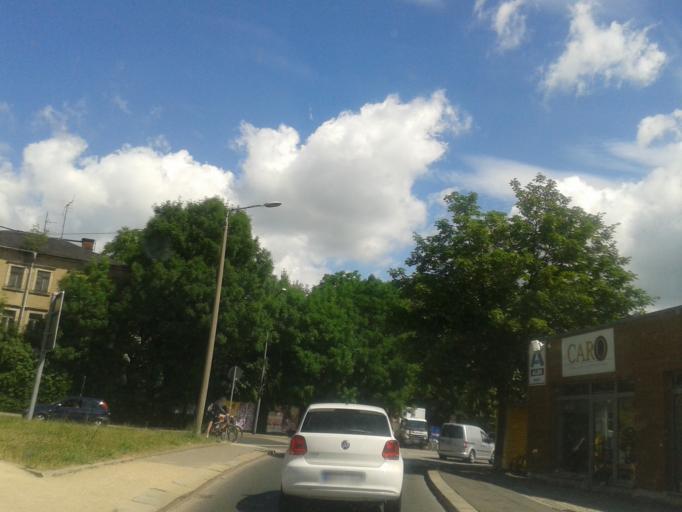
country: DE
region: Saxony
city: Dresden
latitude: 51.0571
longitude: 13.6876
